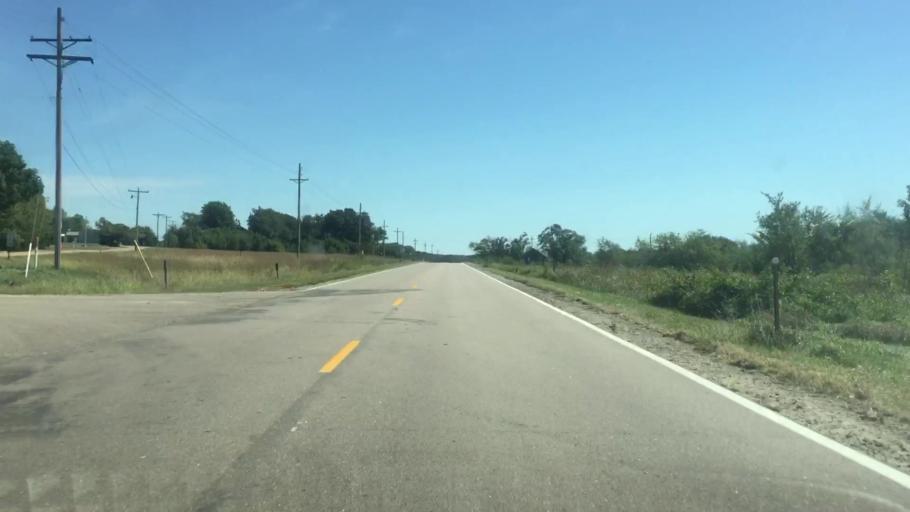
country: US
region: Nebraska
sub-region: Jefferson County
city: Fairbury
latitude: 40.0810
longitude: -97.1026
